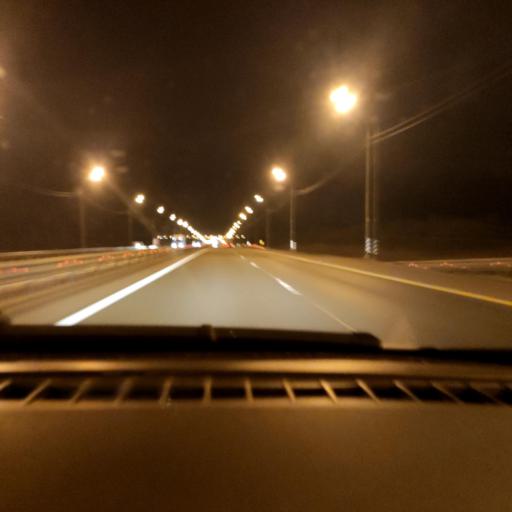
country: RU
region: Lipetsk
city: Khlevnoye
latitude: 52.1935
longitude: 39.1750
